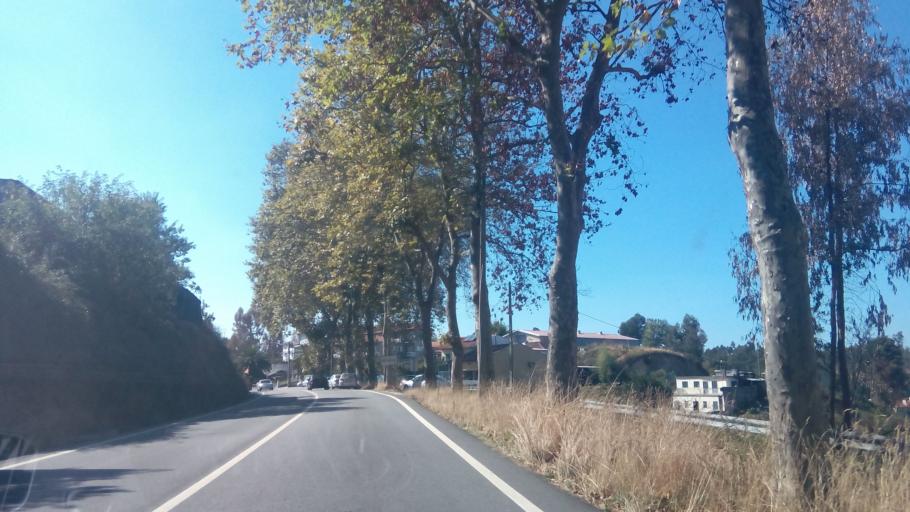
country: PT
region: Porto
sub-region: Lousada
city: Meinedo
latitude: 41.2384
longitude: -8.2198
